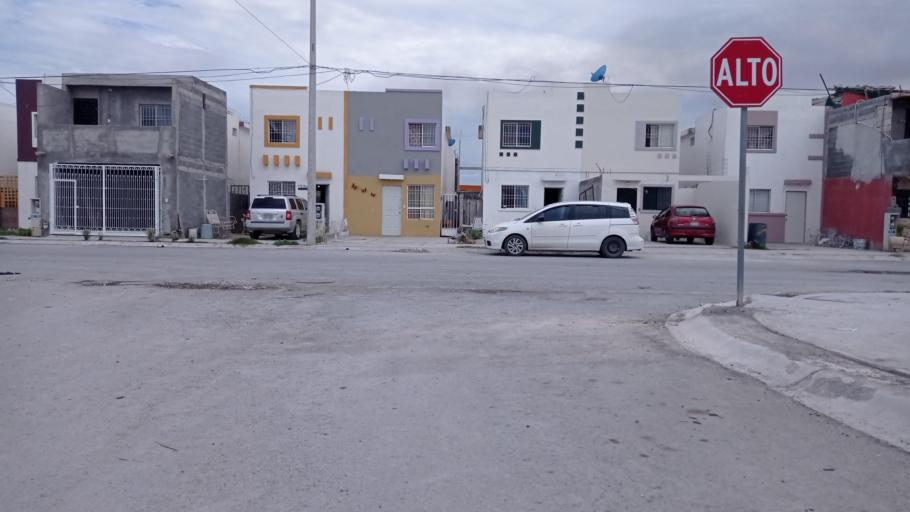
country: MX
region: Nuevo Leon
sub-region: Salinas Victoria
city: Simeprodeso (Colectivo Nuevo)
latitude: 25.8750
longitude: -100.3147
